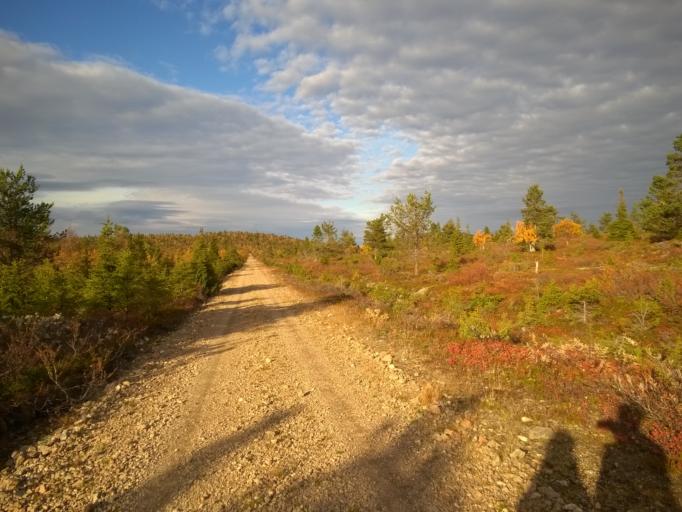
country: FI
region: Lapland
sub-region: Tunturi-Lappi
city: Muonio
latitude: 67.9796
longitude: 24.1059
